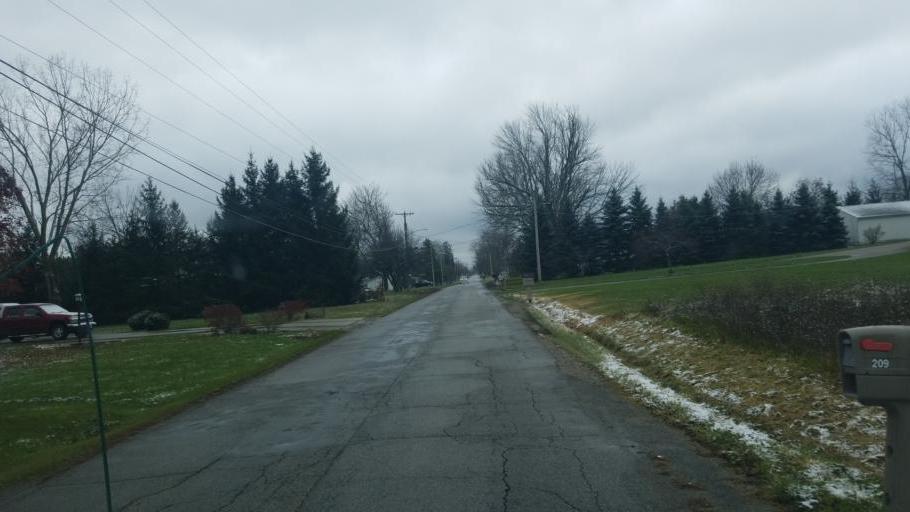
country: US
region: Ohio
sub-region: Richland County
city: Shelby
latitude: 40.8997
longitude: -82.6551
